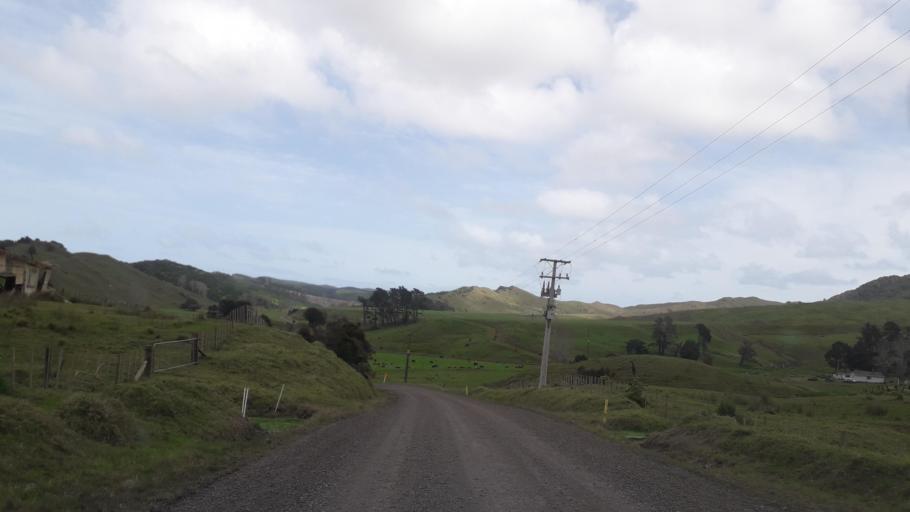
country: NZ
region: Northland
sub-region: Far North District
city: Kaitaia
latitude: -35.4148
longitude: 173.3656
